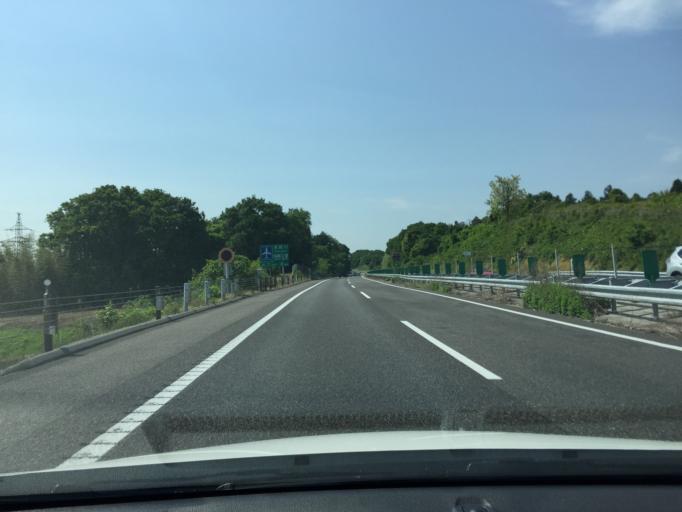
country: JP
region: Fukushima
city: Sukagawa
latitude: 37.3185
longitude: 140.3431
